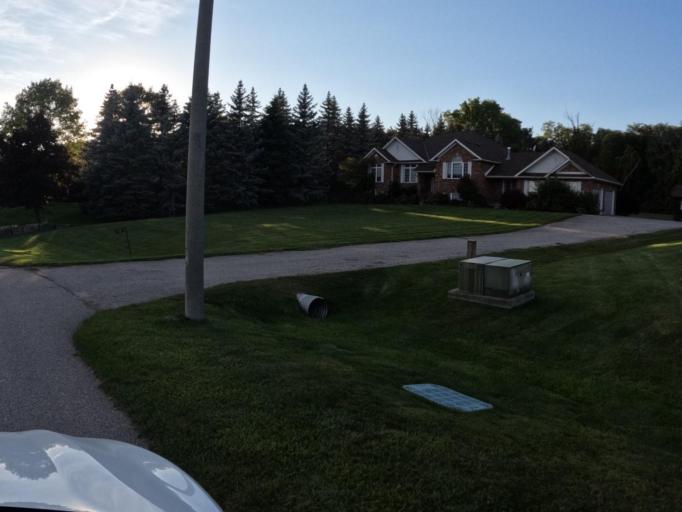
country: CA
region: Ontario
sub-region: Wellington County
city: Guelph
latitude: 43.4485
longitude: -80.1225
